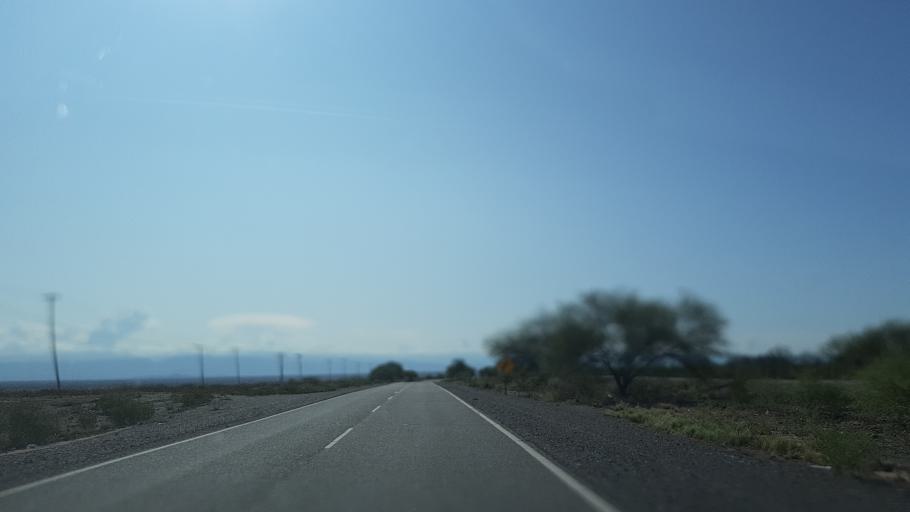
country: AR
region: San Juan
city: Caucete
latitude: -31.7552
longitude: -68.0804
